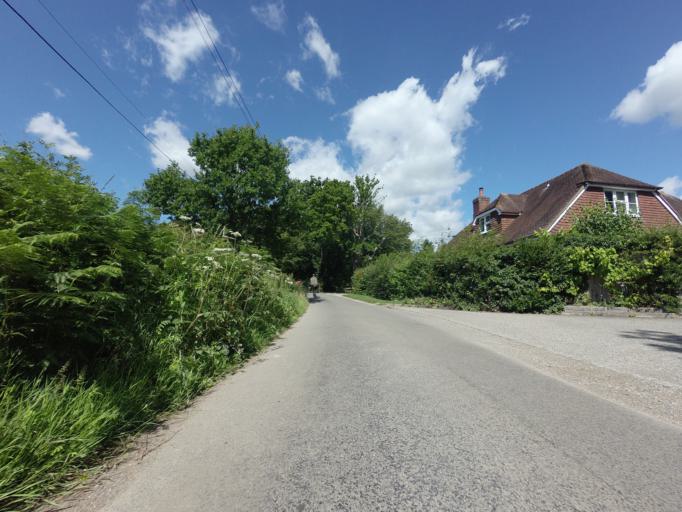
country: GB
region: England
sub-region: East Sussex
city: Horam
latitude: 50.9118
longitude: 0.1982
